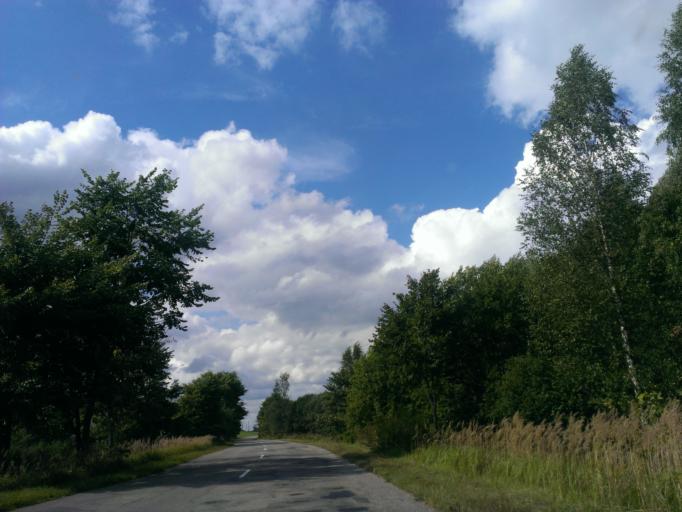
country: LV
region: Ropazu
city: Ropazi
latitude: 56.9608
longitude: 24.5415
